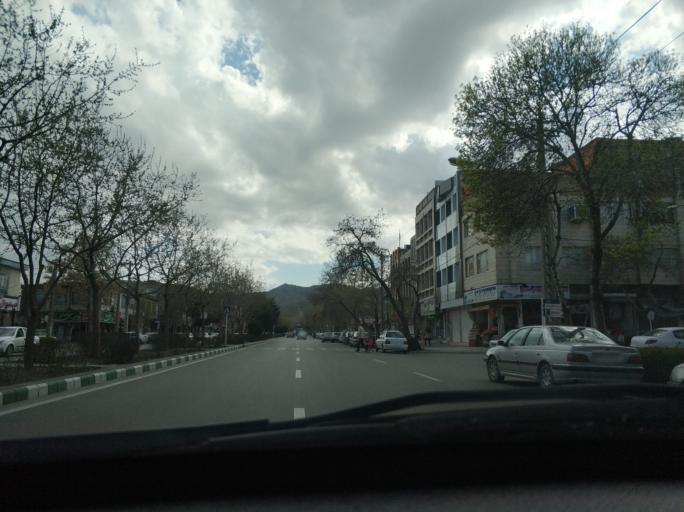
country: IR
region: Razavi Khorasan
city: Mashhad
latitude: 36.2697
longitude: 59.5886
